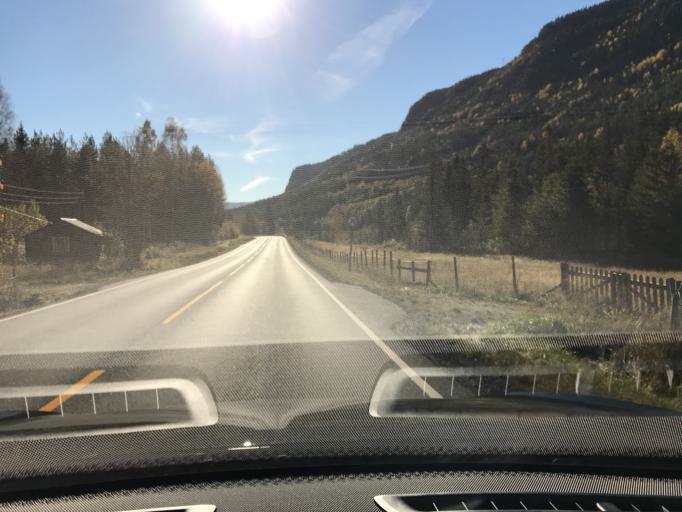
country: NO
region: Buskerud
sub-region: Gol
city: Gol
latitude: 60.6719
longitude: 9.0329
